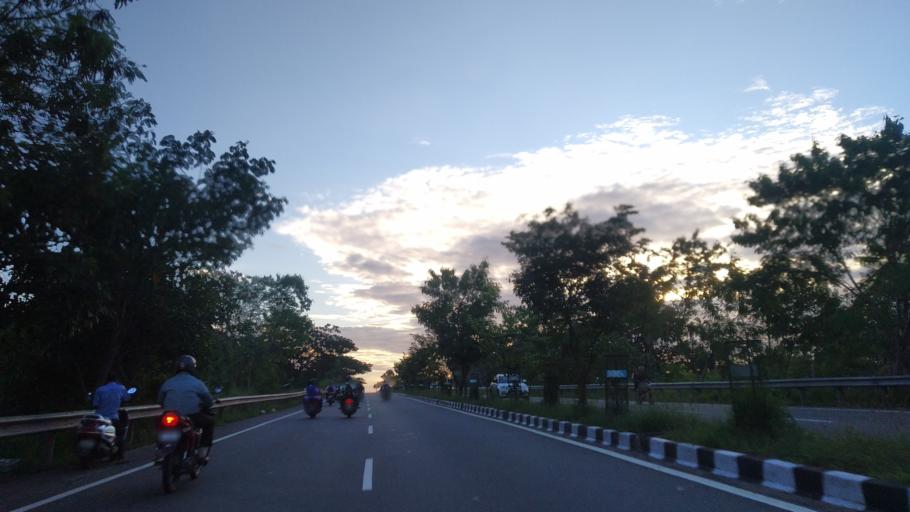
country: IN
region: Kerala
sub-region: Ernakulam
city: Elur
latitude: 10.0683
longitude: 76.3008
